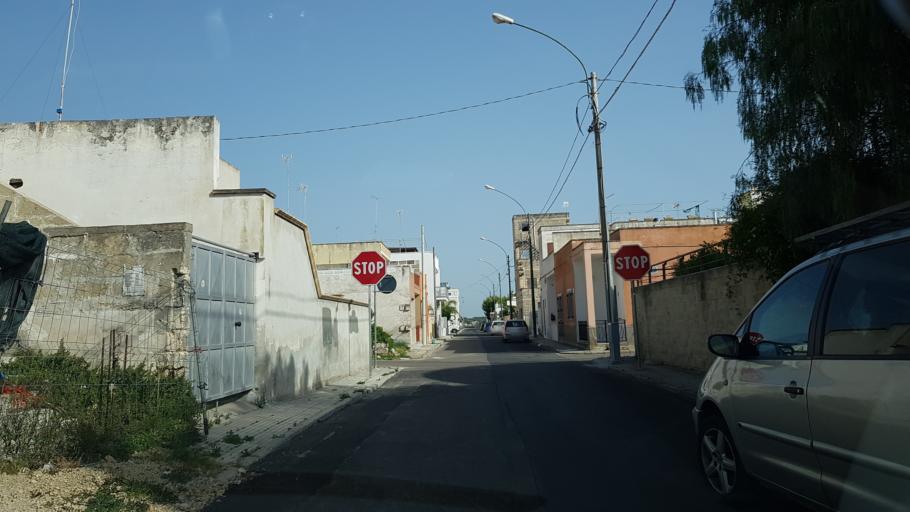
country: IT
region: Apulia
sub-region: Provincia di Lecce
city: Porto Cesareo
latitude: 40.2597
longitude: 17.9016
